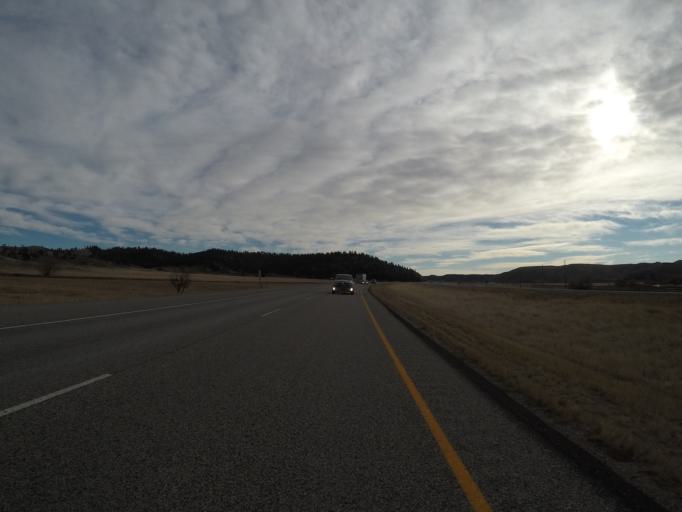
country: US
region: Montana
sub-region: Stillwater County
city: Columbus
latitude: 45.6910
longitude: -109.3633
